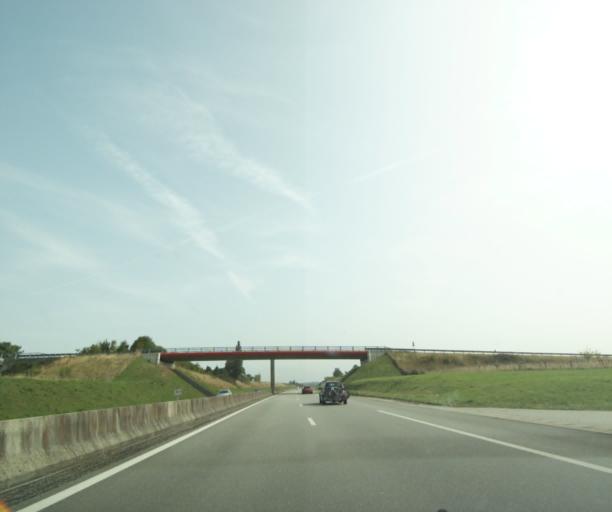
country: FR
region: Lower Normandy
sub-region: Departement de l'Orne
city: Radon
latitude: 48.5163
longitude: 0.1400
